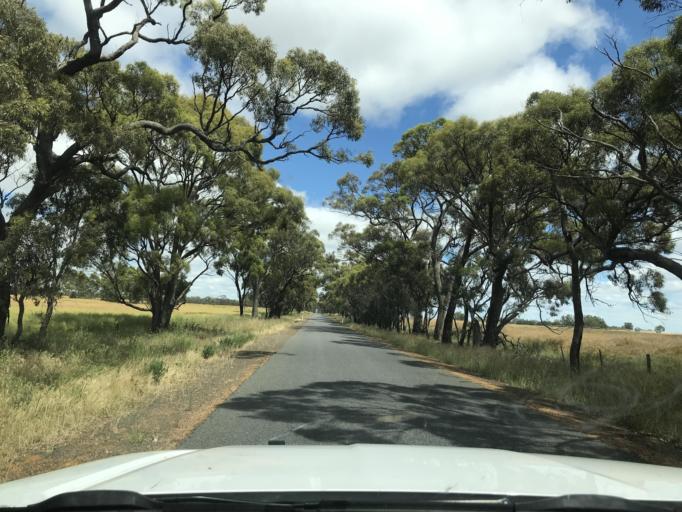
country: AU
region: South Australia
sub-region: Naracoorte and Lucindale
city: Naracoorte
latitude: -36.6836
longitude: 141.3156
